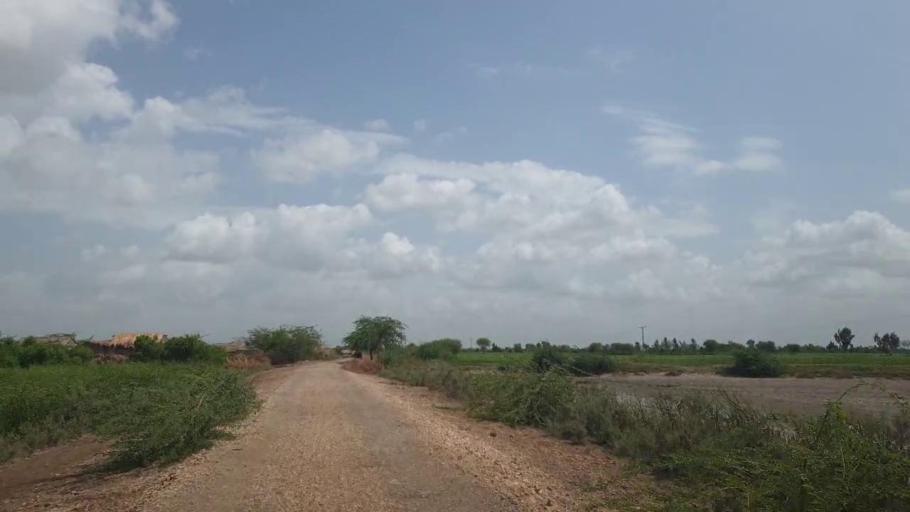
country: PK
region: Sindh
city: Tando Bago
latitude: 24.6564
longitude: 68.9927
